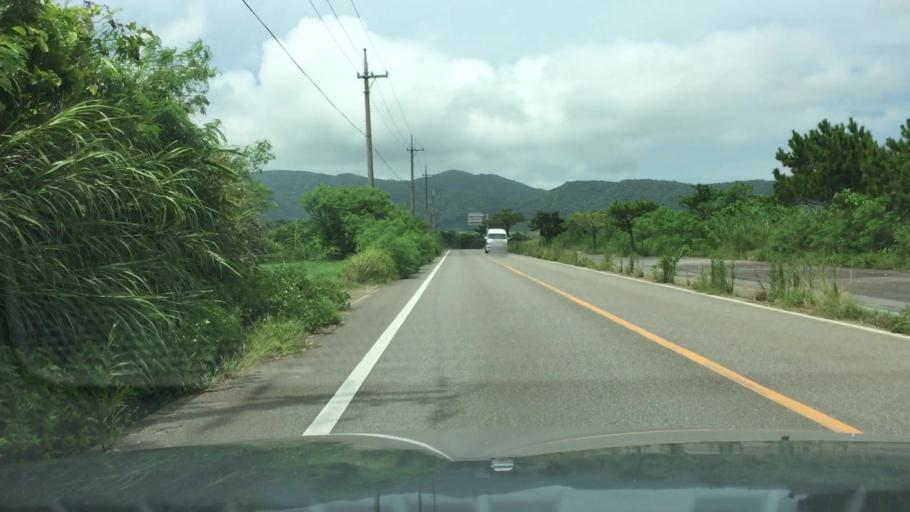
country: JP
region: Okinawa
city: Ishigaki
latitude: 24.4116
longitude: 124.2141
